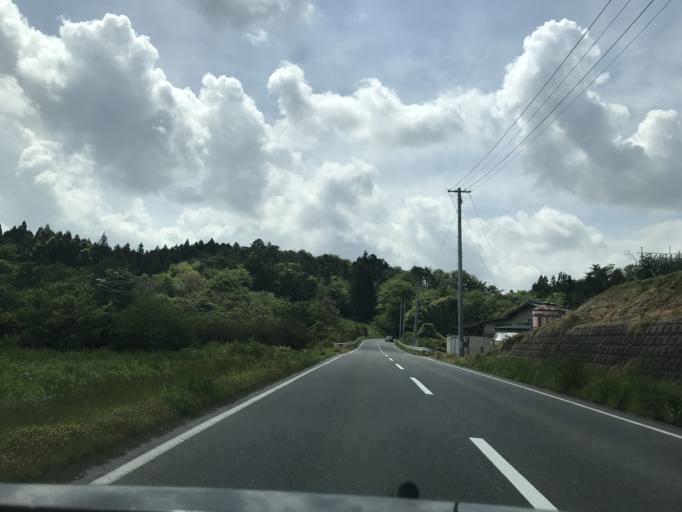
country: JP
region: Iwate
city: Ichinoseki
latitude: 38.7865
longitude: 141.0007
